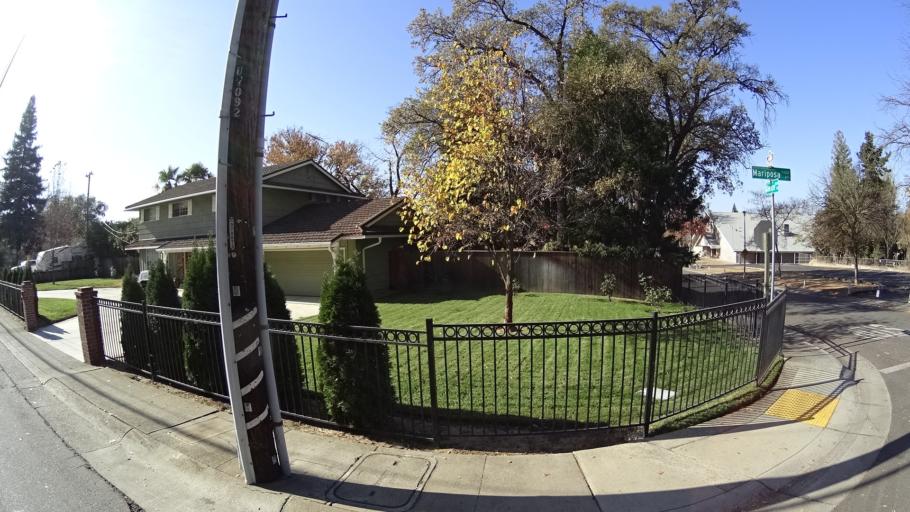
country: US
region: California
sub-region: Sacramento County
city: Citrus Heights
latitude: 38.6946
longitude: -121.2812
